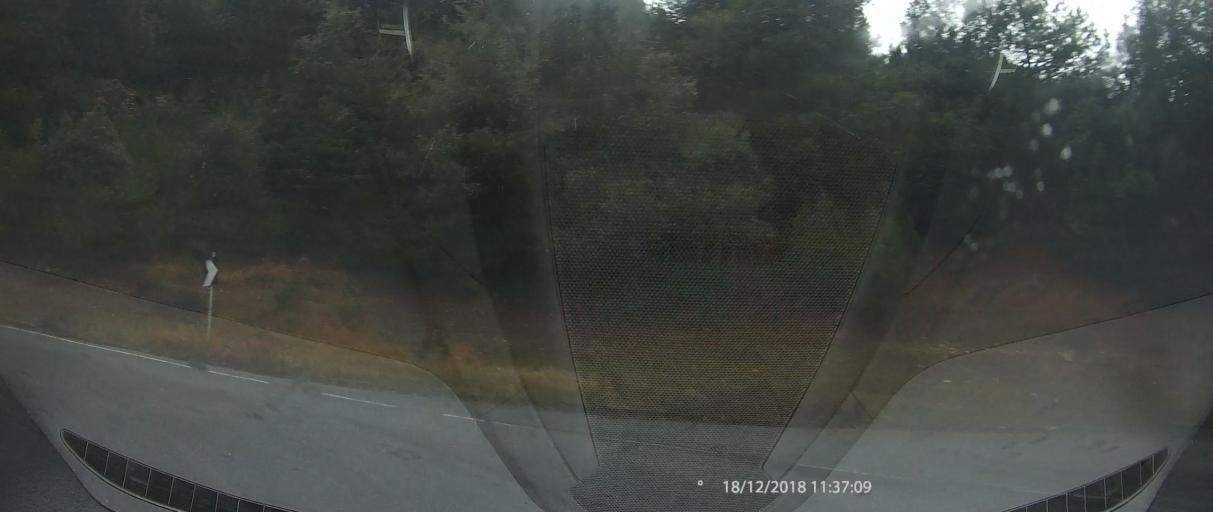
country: GR
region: Central Macedonia
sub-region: Nomos Pierias
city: Litochoro
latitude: 40.1185
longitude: 22.4780
